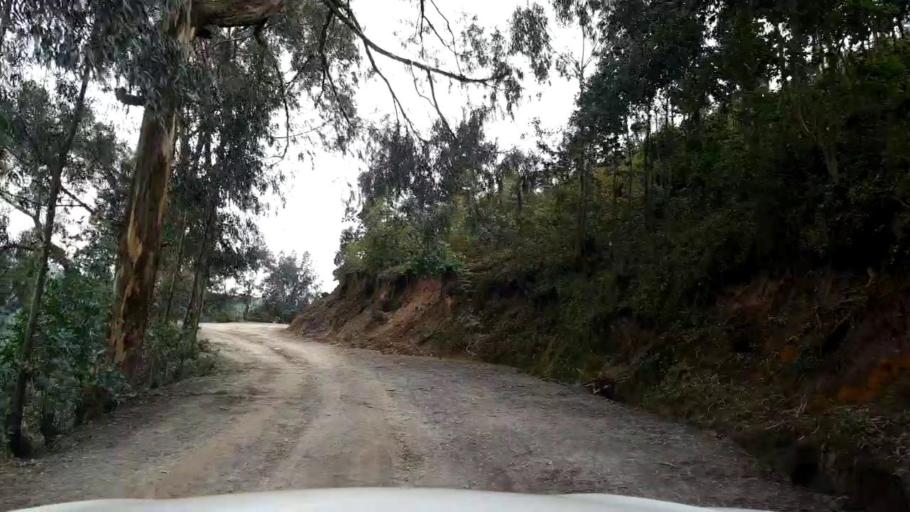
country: RW
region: Western Province
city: Kibuye
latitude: -1.9600
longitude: 29.4769
